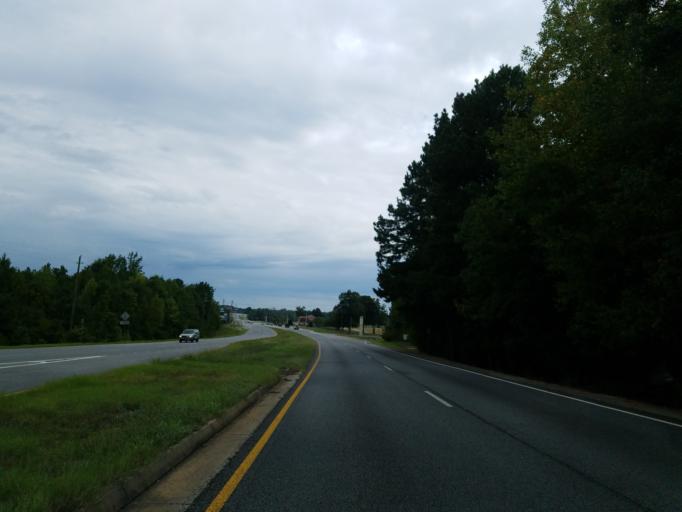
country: US
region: Georgia
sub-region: Henry County
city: Hampton
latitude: 33.3935
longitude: -84.3107
